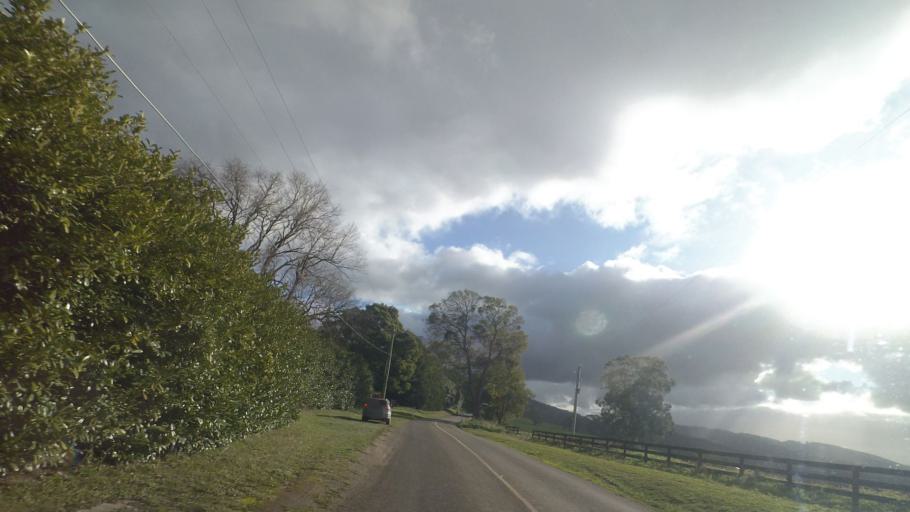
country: AU
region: Victoria
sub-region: Cardinia
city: Emerald
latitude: -37.9099
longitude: 145.4319
